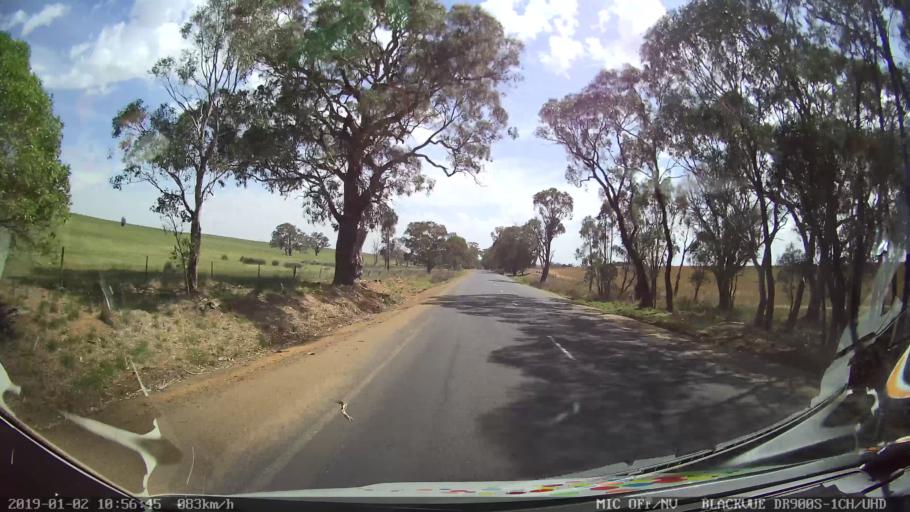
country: AU
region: New South Wales
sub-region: Cootamundra
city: Cootamundra
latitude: -34.6434
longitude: 148.2788
